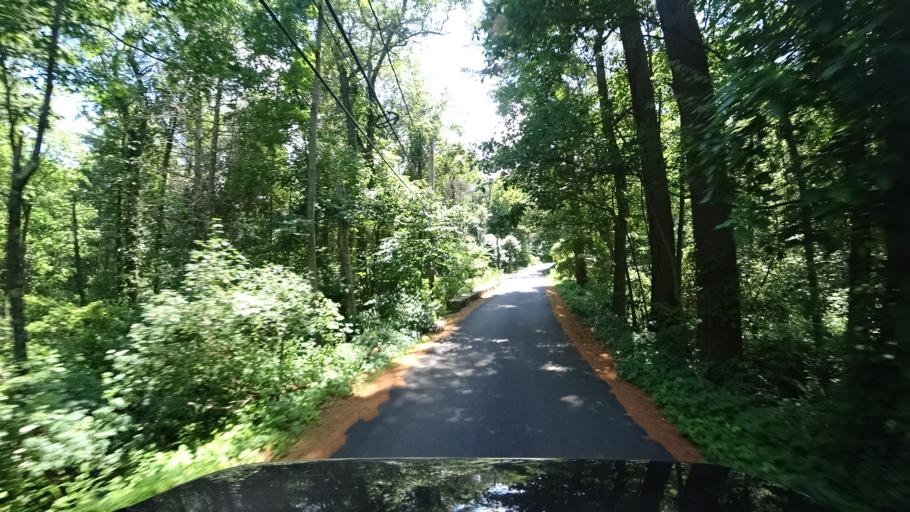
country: US
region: Massachusetts
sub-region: Norfolk County
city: Dedham
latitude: 42.2513
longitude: -71.1968
